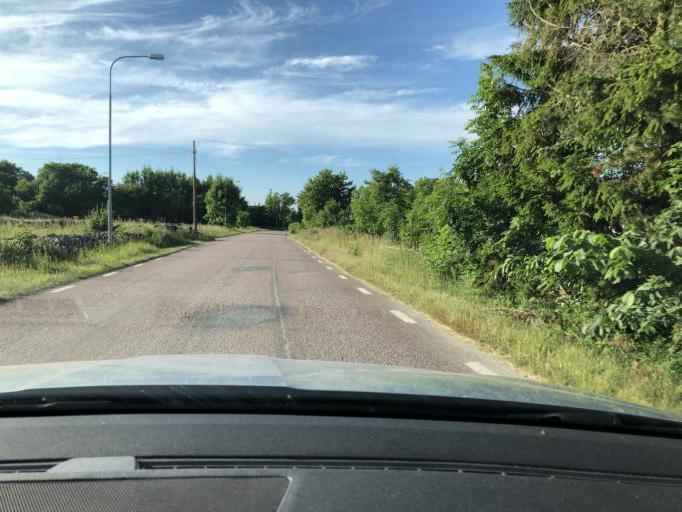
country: SE
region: Blekinge
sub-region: Solvesborgs Kommun
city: Soelvesborg
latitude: 56.1487
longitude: 14.6032
